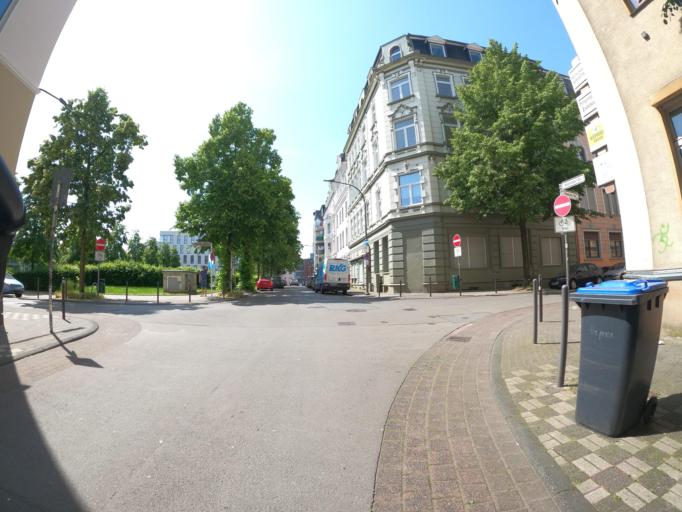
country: DE
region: North Rhine-Westphalia
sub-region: Regierungsbezirk Dusseldorf
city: Wuppertal
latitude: 51.2657
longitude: 7.1523
